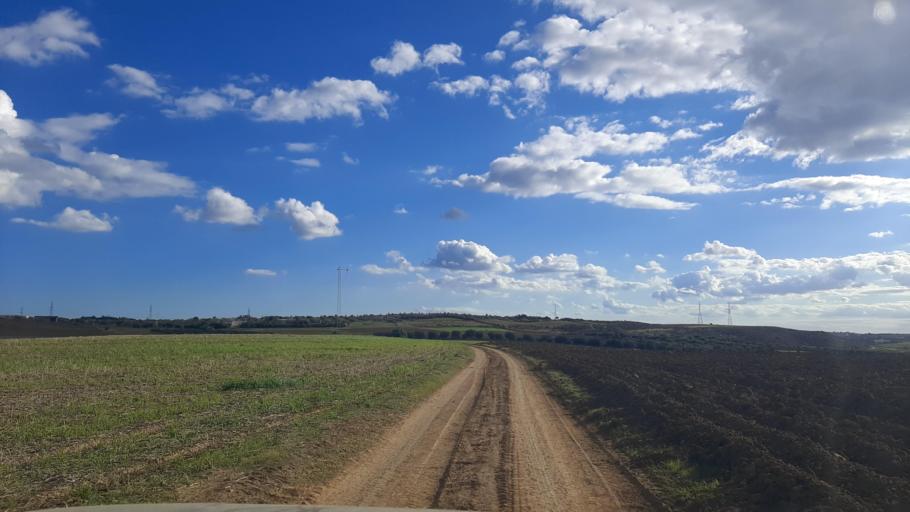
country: TN
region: Nabul
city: Bu `Urqub
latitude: 36.4483
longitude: 10.5013
